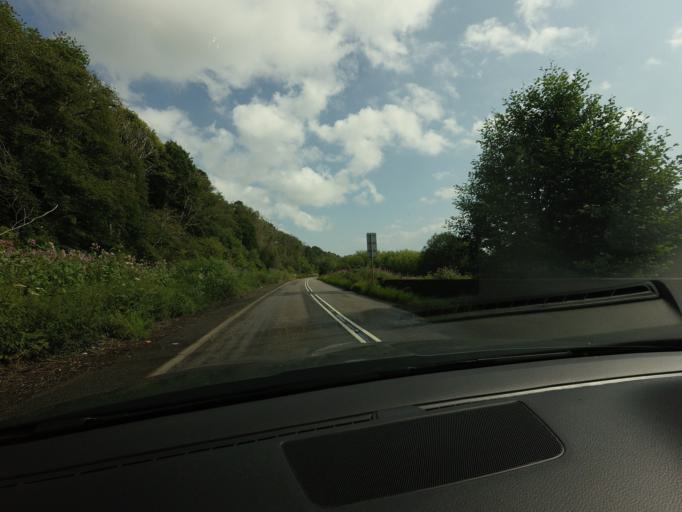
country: GB
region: Scotland
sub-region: Highland
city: Dingwall
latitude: 57.6055
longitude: -4.4185
